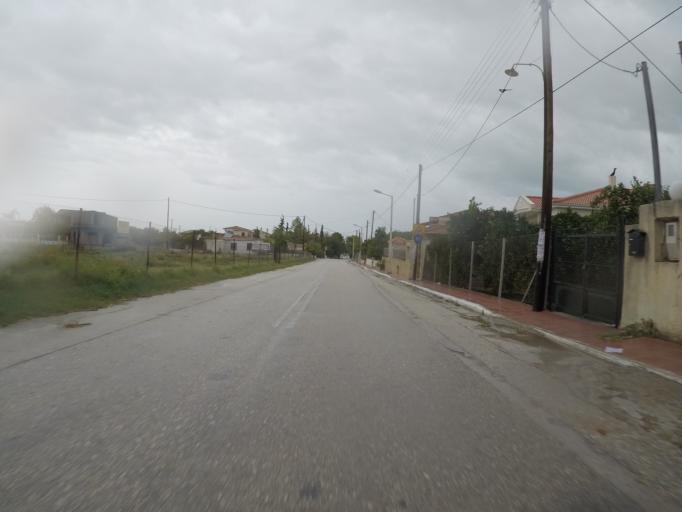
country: GR
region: Peloponnese
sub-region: Nomos Korinthias
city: Arkhaia Korinthos
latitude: 37.9045
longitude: 22.8849
